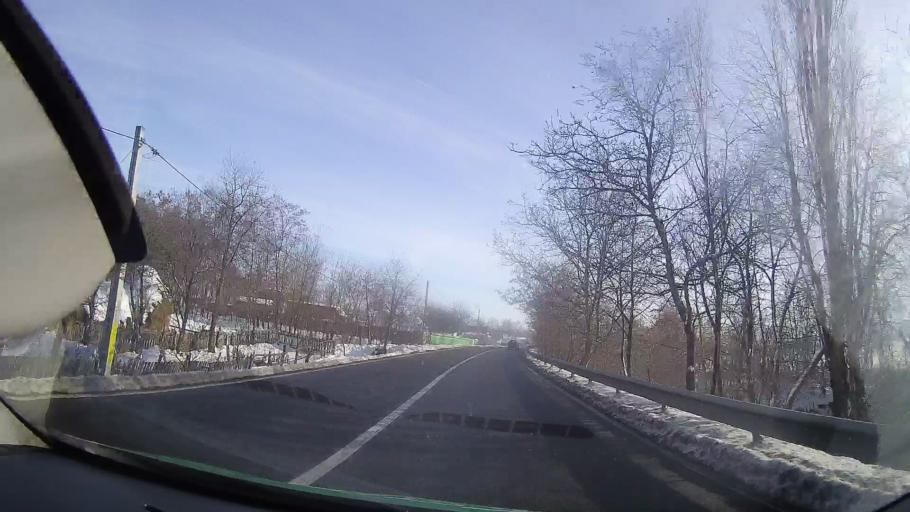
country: RO
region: Neamt
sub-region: Comuna Ghindaoani
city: Ghindaoani
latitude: 47.0727
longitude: 26.3607
